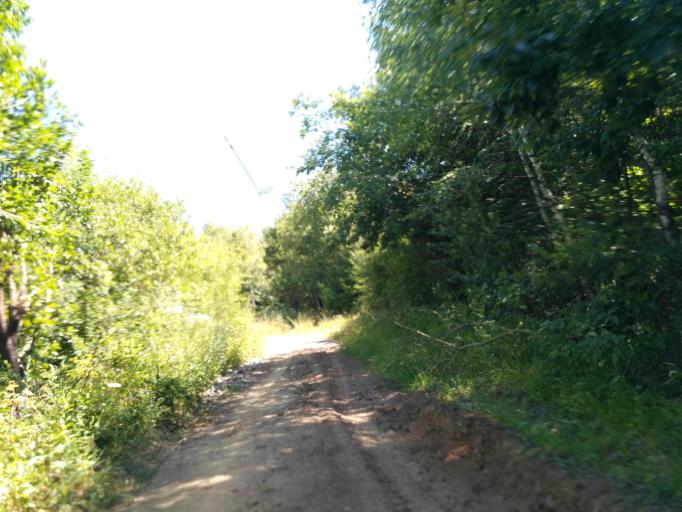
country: PL
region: Subcarpathian Voivodeship
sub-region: Powiat sanocki
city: Bukowsko
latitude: 49.4881
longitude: 22.0836
